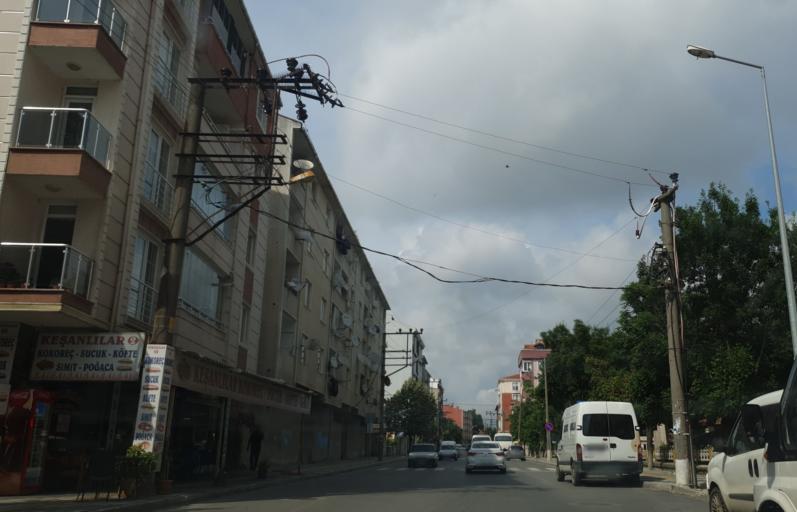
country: TR
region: Tekirdag
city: Saray
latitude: 41.4445
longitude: 27.9258
